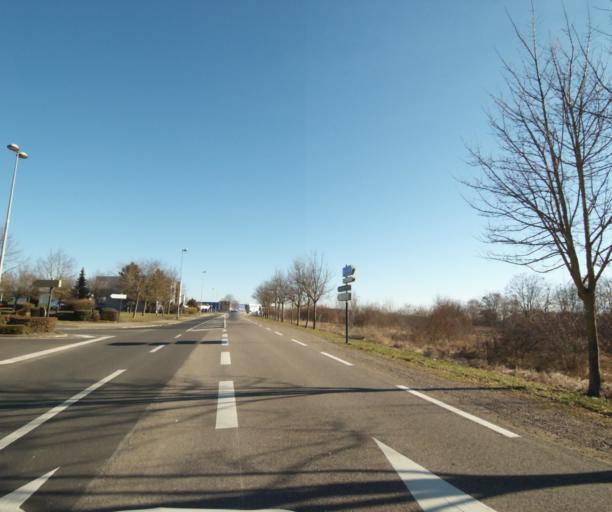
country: FR
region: Lorraine
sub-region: Departement de Meurthe-et-Moselle
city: Laxou
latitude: 48.7037
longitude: 6.1310
